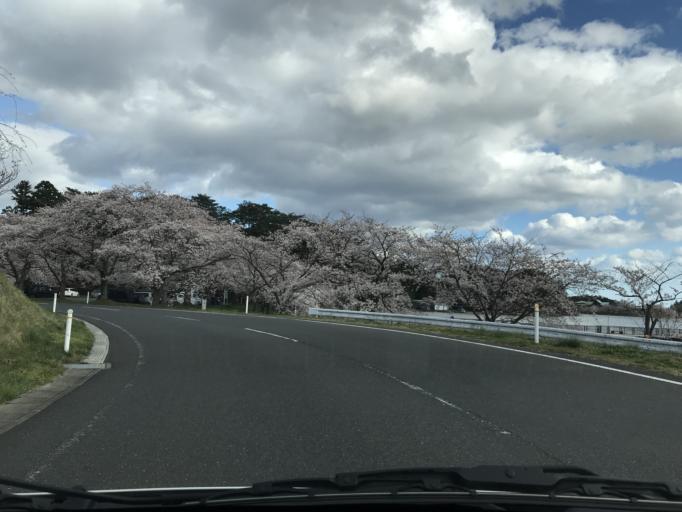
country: JP
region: Miyagi
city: Wakuya
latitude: 38.6162
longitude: 141.2353
